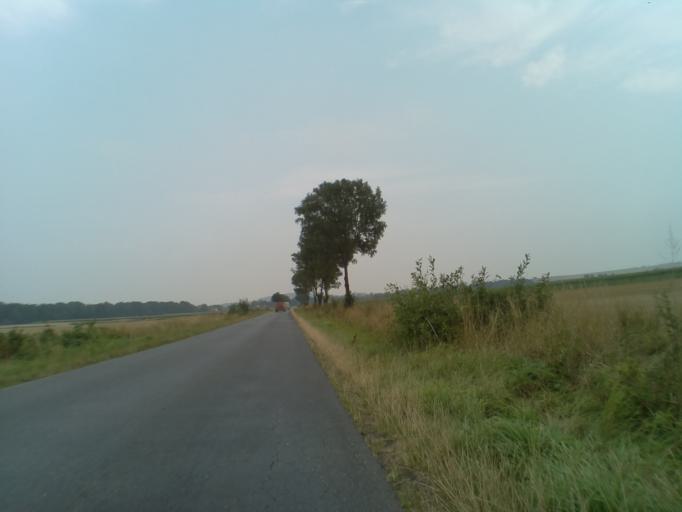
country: PL
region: Lower Silesian Voivodeship
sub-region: Powiat swidnicki
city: Strzegom
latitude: 50.9238
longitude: 16.3232
